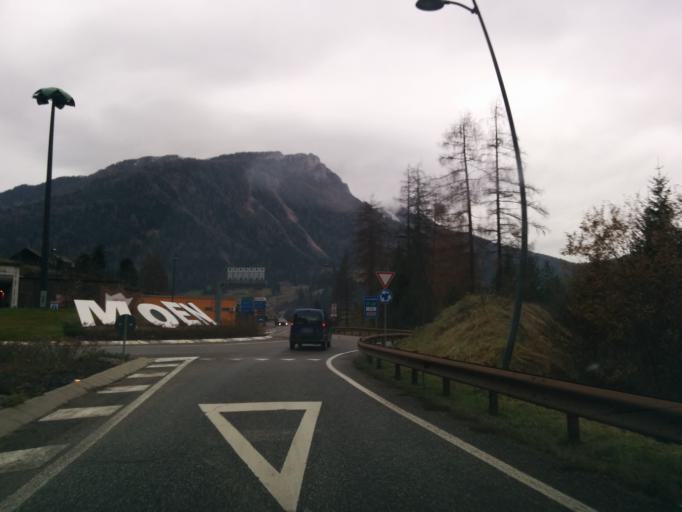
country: IT
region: Trentino-Alto Adige
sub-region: Provincia di Trento
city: Moena
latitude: 46.3744
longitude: 11.6672
